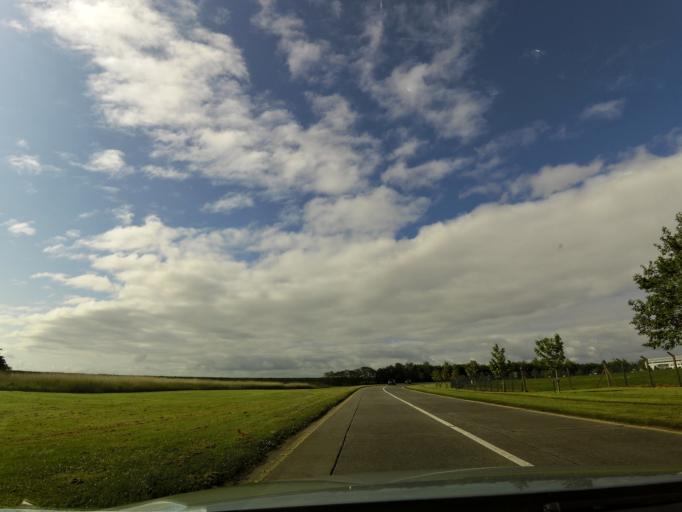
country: IE
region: Munster
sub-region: An Clar
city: Shannon
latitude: 52.6936
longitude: -8.9028
